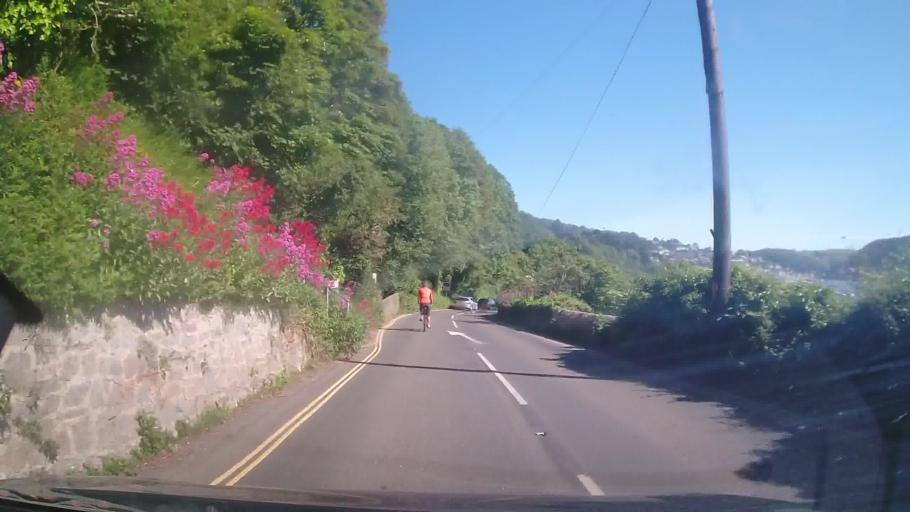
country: GB
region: England
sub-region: Devon
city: Dartmouth
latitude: 50.3617
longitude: -3.5740
